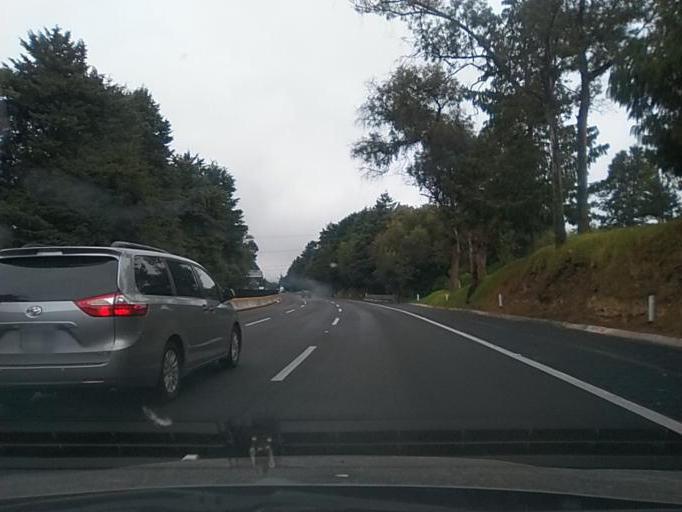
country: MX
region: Mexico City
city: Xochimilco
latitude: 19.1789
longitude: -99.1550
